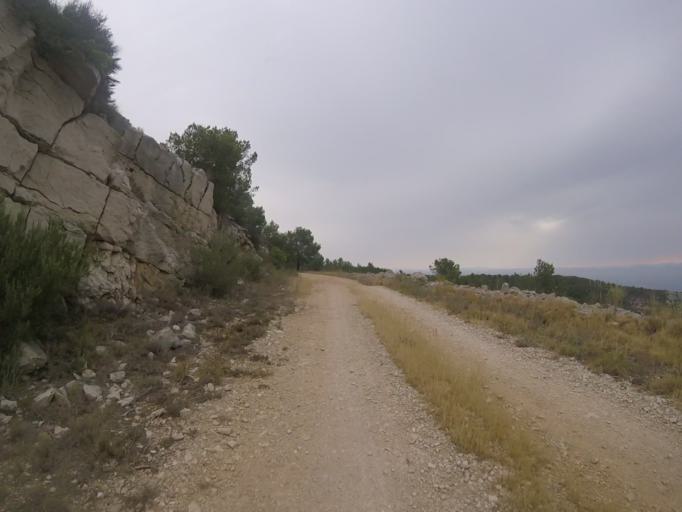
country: ES
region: Valencia
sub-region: Provincia de Castello
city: Alcoceber
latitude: 40.2803
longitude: 0.2832
